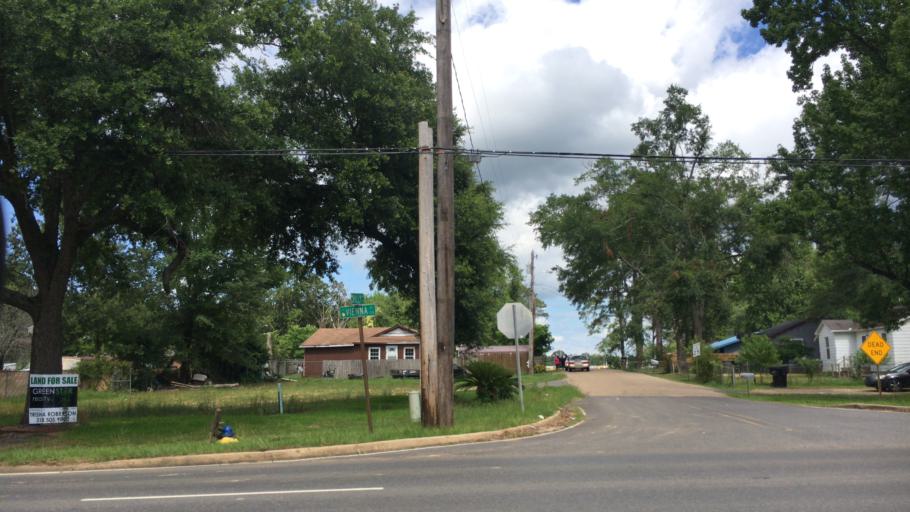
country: US
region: Louisiana
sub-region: Lincoln Parish
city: Ruston
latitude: 32.5105
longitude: -92.6377
